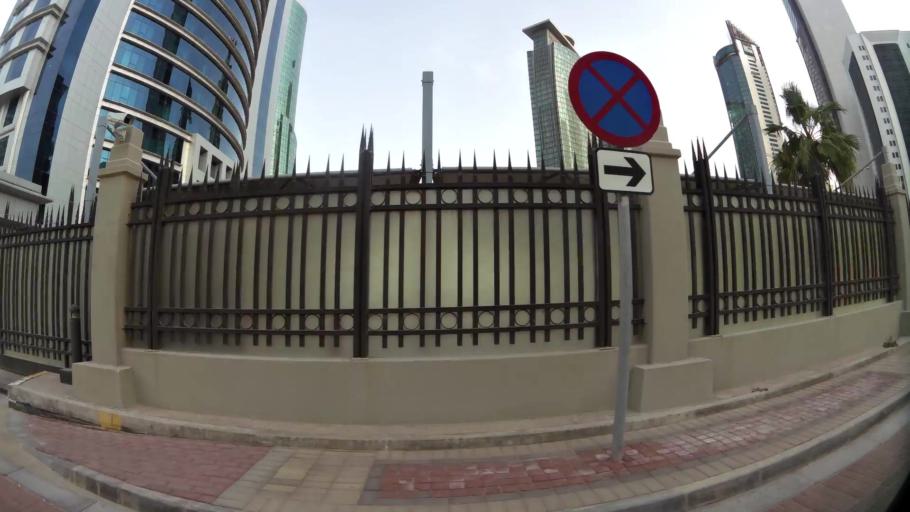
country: QA
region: Baladiyat ad Dawhah
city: Doha
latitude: 25.3275
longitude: 51.5269
